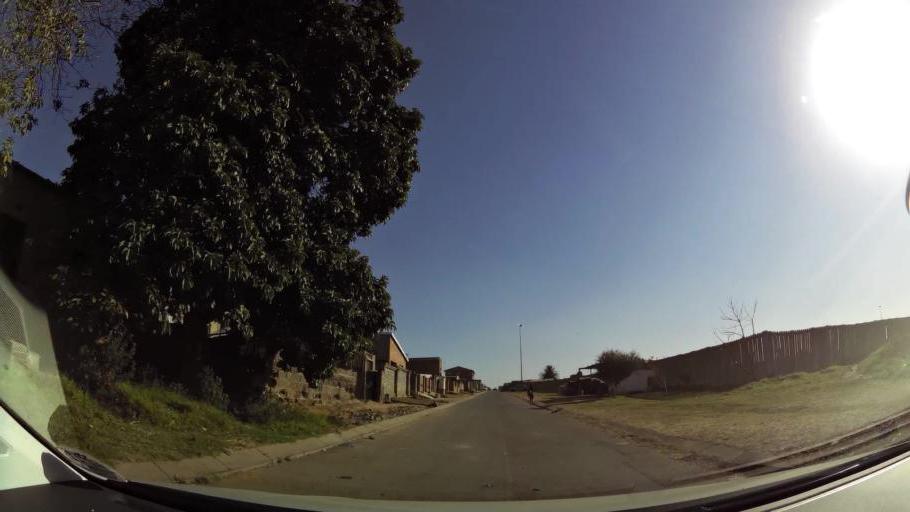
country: ZA
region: Gauteng
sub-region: Ekurhuleni Metropolitan Municipality
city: Tembisa
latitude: -26.0154
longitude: 28.2353
